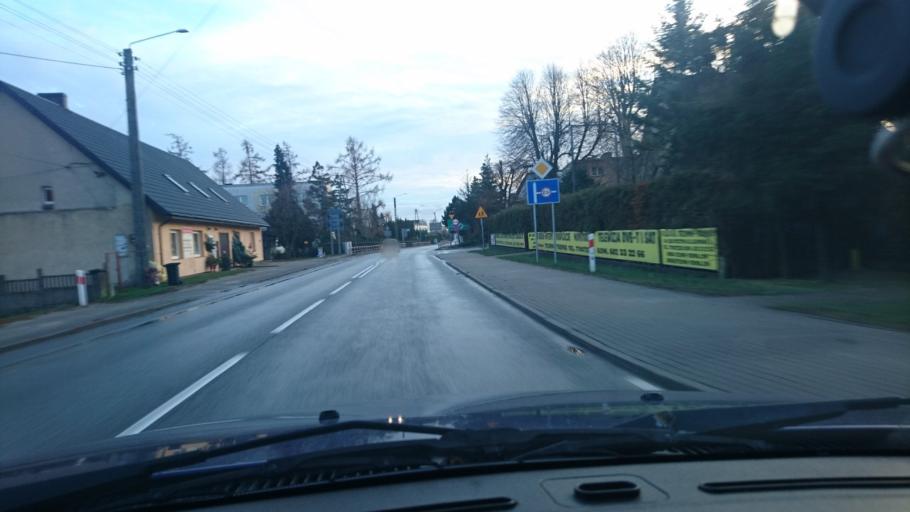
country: PL
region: Opole Voivodeship
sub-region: Powiat kluczborski
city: Byczyna
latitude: 51.1159
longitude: 18.2093
